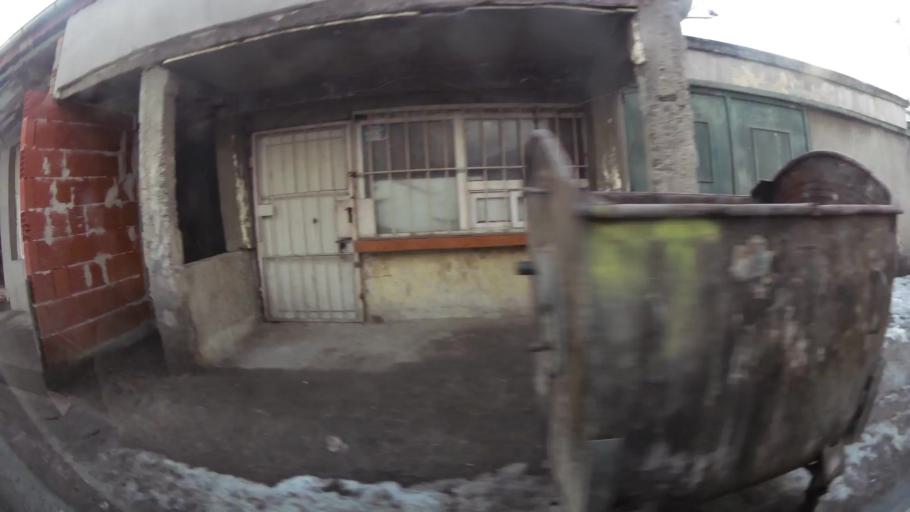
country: BG
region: Sofia-Capital
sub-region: Stolichna Obshtina
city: Sofia
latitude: 42.6959
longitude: 23.2667
